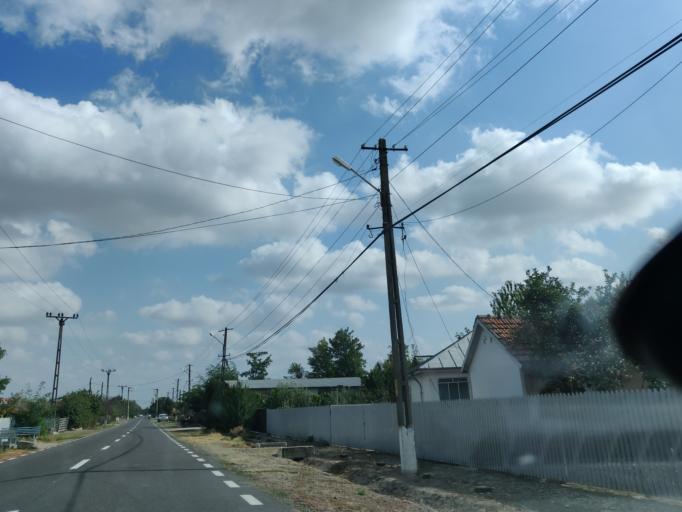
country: RO
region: Vrancea
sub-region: Comuna Ciorasti
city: Ciorasti
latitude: 45.4264
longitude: 27.2897
